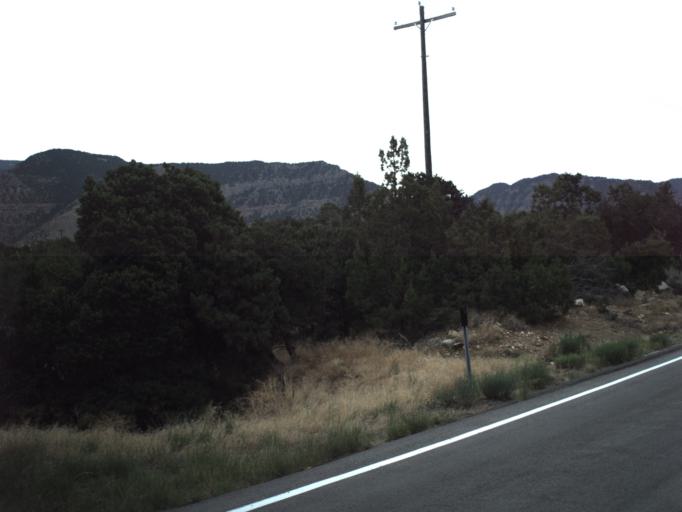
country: US
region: Utah
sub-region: Carbon County
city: East Carbon City
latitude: 39.5335
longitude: -110.4030
